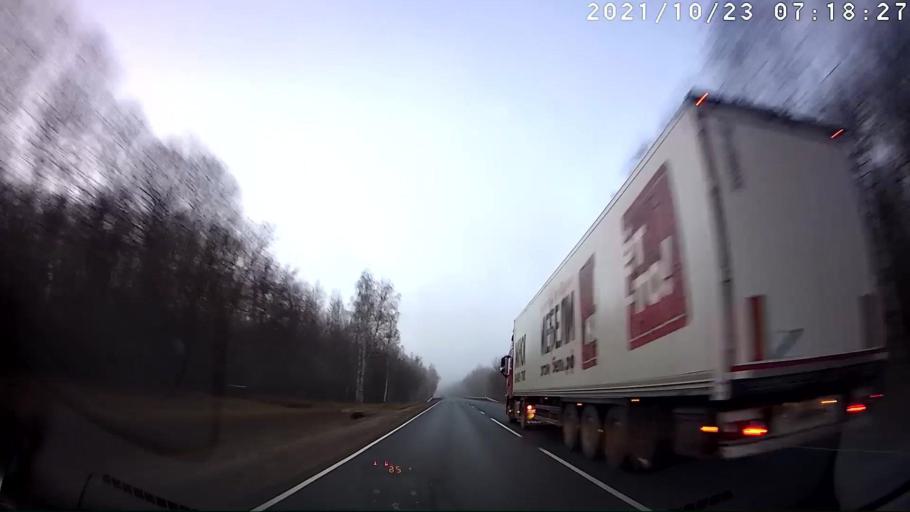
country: RU
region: Saratov
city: Khvalynsk
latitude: 52.4524
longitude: 48.0130
